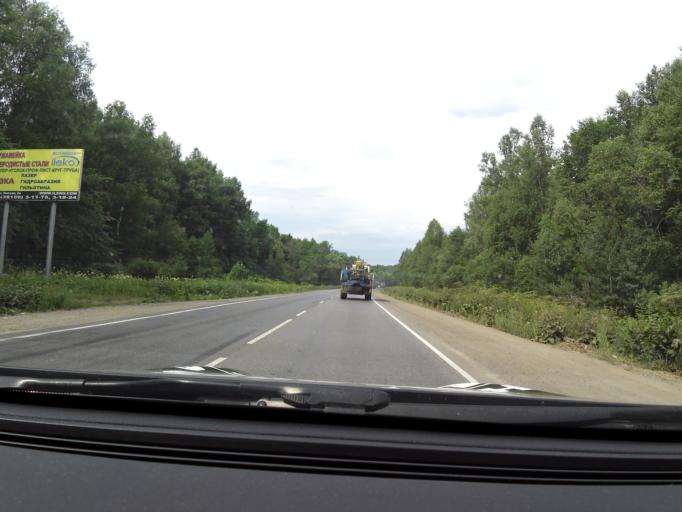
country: RU
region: Chelyabinsk
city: Asha
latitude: 54.8868
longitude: 57.2951
